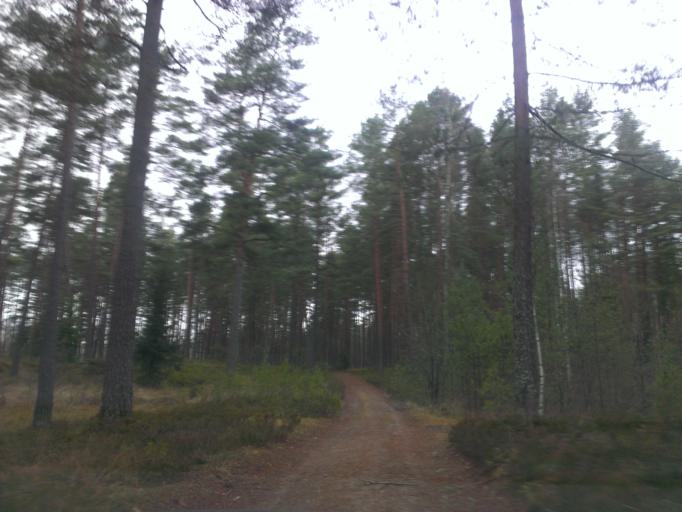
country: LV
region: Riga
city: Bergi
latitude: 57.0069
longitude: 24.3477
